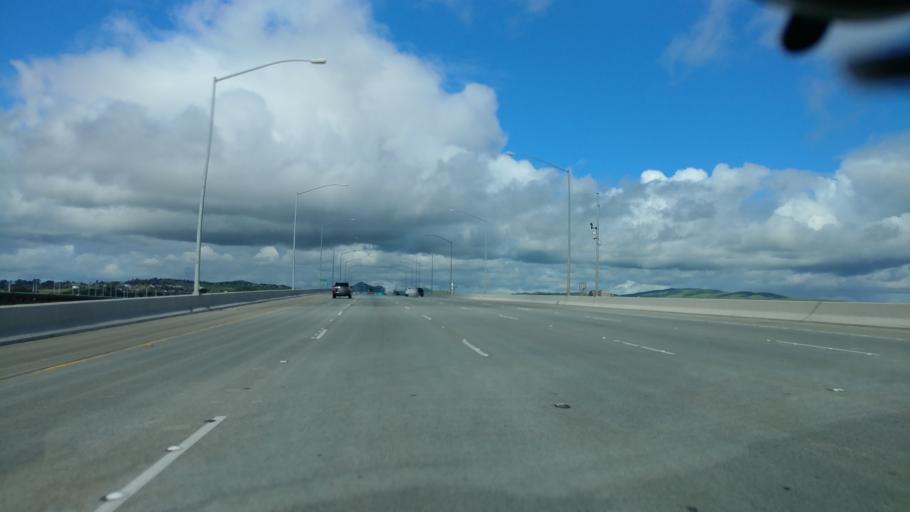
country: US
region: California
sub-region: Contra Costa County
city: Martinez
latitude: 38.0379
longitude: -122.1183
